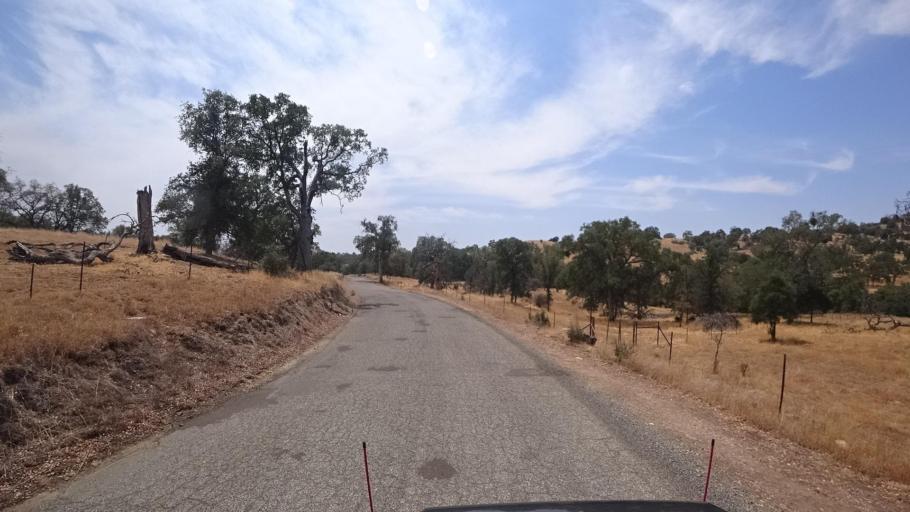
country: US
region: California
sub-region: Mariposa County
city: Mariposa
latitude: 37.3853
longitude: -119.8724
